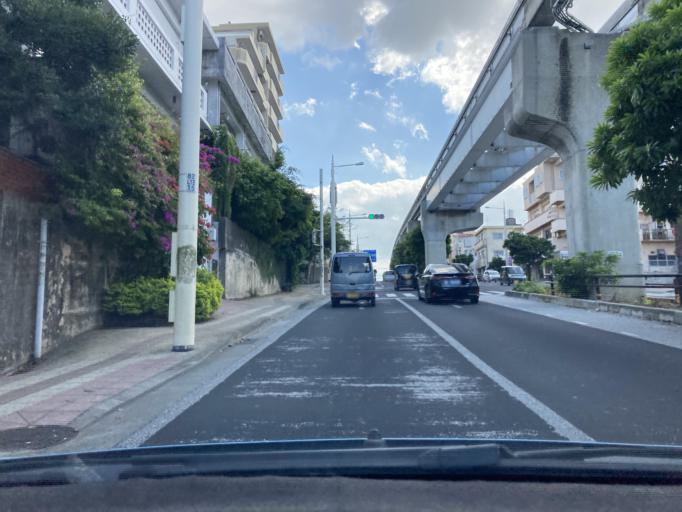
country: JP
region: Okinawa
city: Naha-shi
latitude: 26.2219
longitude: 127.7219
